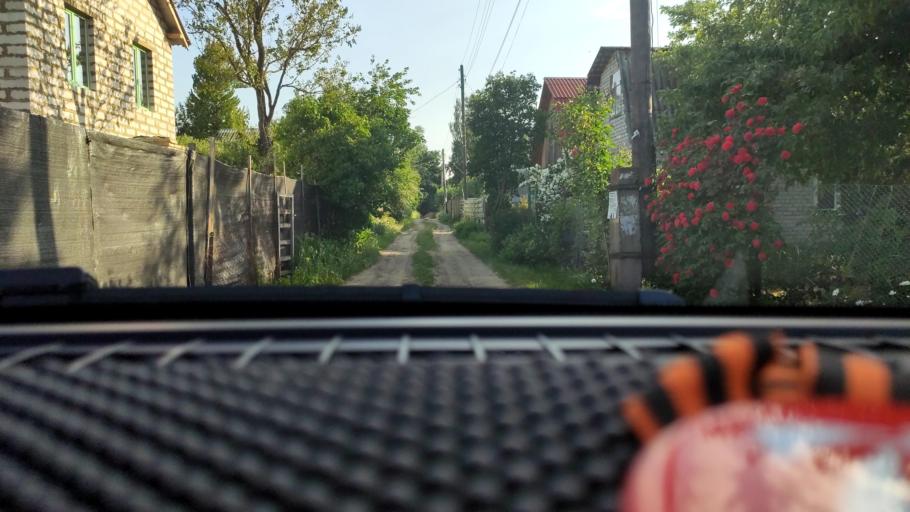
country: RU
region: Voronezj
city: Maslovka
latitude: 51.5933
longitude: 39.1690
